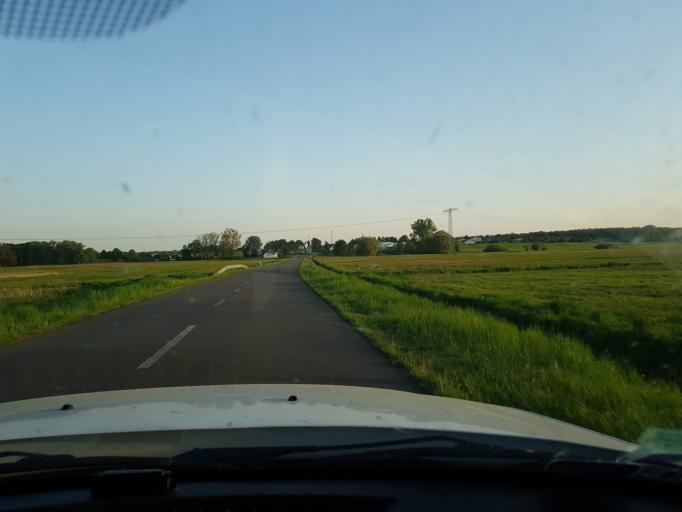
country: PL
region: West Pomeranian Voivodeship
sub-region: Powiat stargardzki
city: Kobylanka
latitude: 53.3615
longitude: 14.8554
